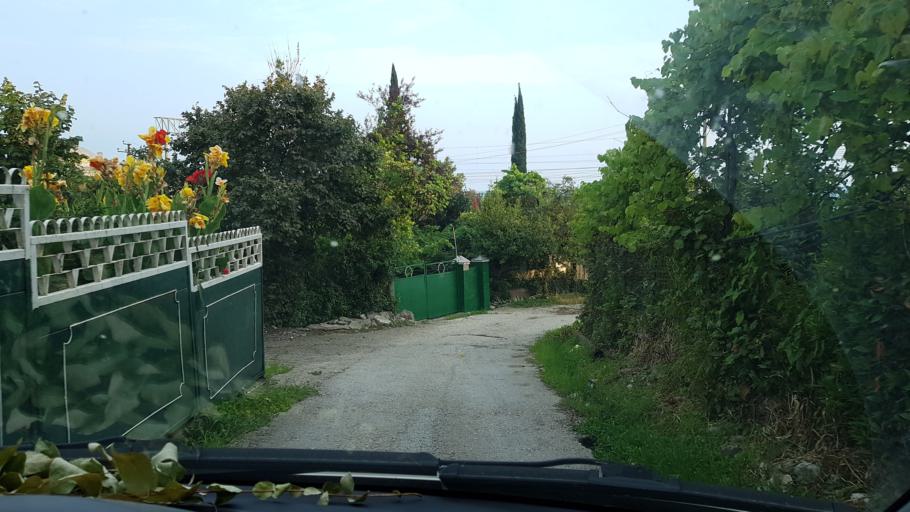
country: GE
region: Abkhazia
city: Stantsiya Novyy Afon
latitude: 43.0822
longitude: 40.8374
